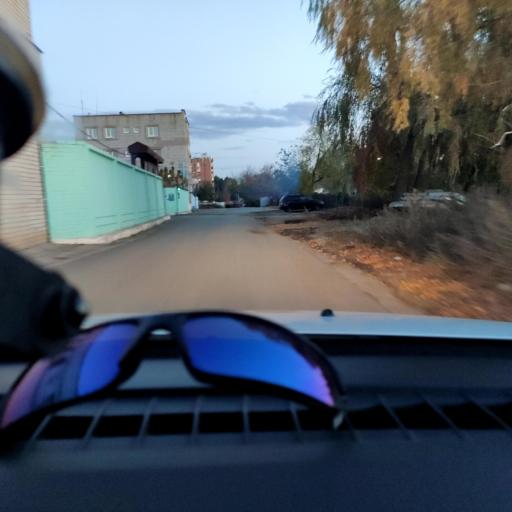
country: RU
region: Samara
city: Samara
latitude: 53.2258
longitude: 50.2249
